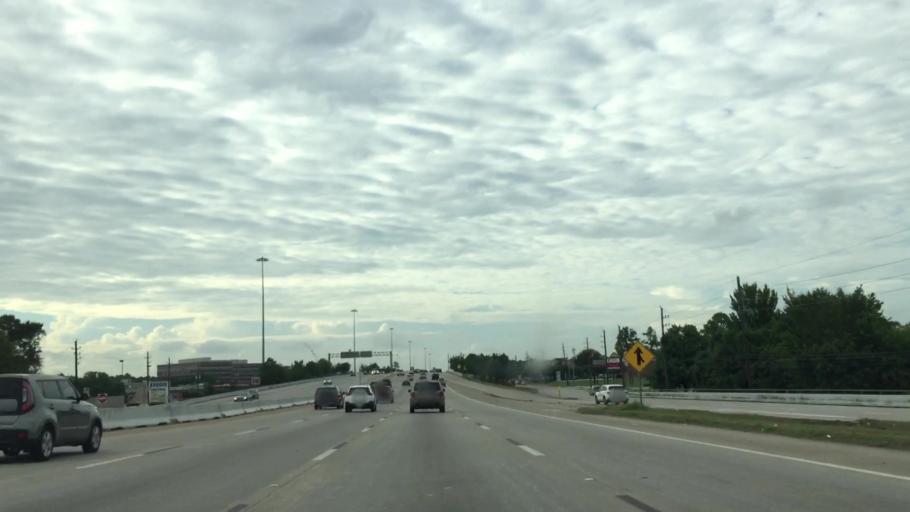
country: US
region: Texas
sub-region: Harris County
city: Oak Cliff Place
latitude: 29.9851
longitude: -95.5704
